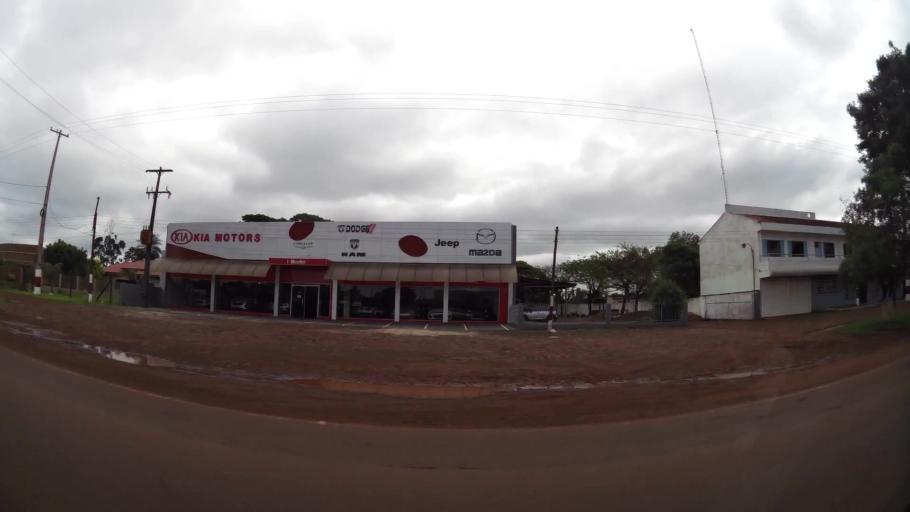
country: PY
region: Alto Parana
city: Ciudad del Este
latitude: -25.3845
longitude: -54.6426
